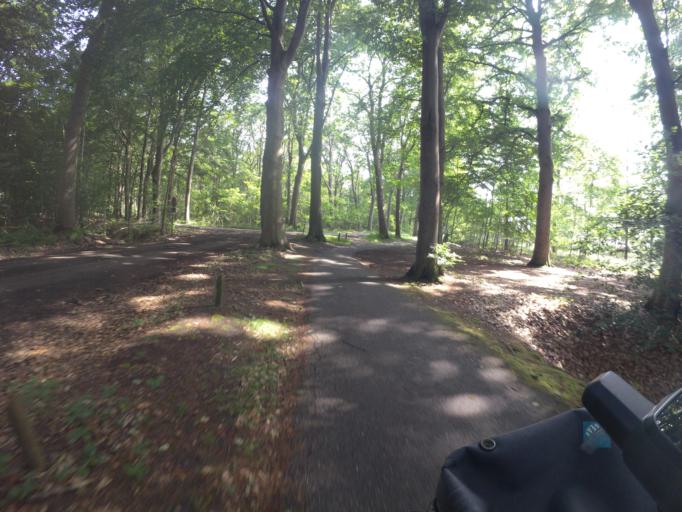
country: NL
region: Friesland
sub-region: Gemeente Weststellingwerf
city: Noordwolde
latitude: 52.8822
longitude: 6.2154
